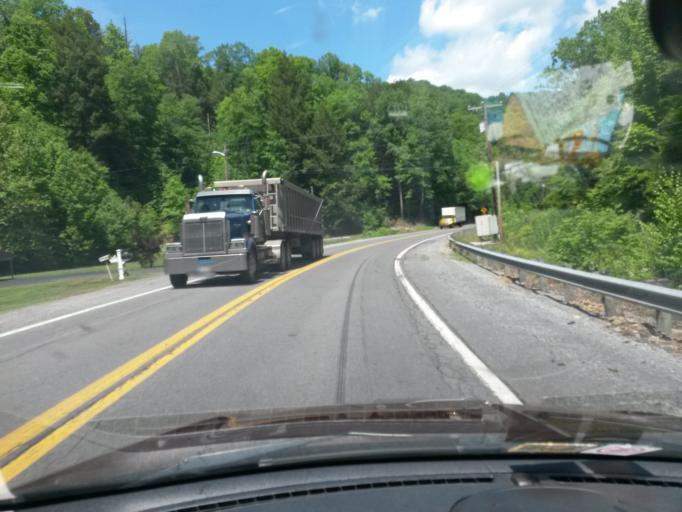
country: US
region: West Virginia
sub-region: Wyoming County
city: Pineville
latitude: 37.5035
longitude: -81.5397
